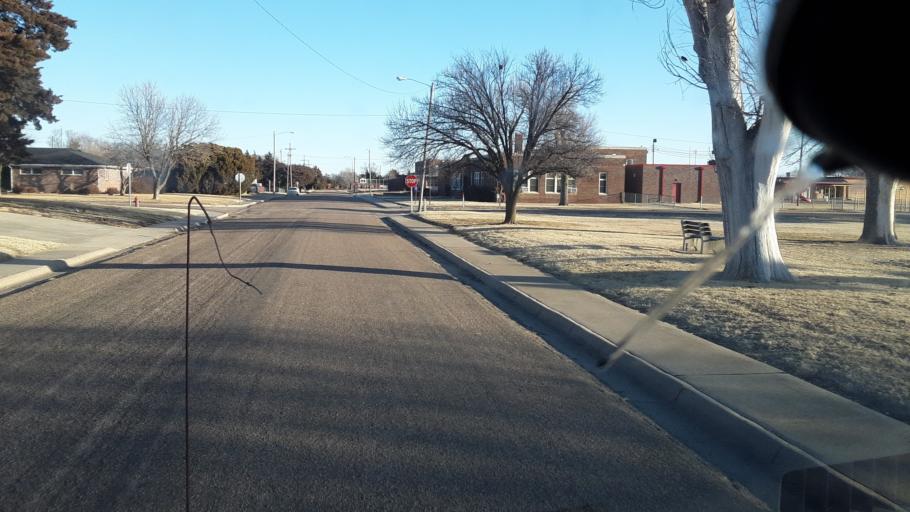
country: US
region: Kansas
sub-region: Rice County
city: Lyons
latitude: 38.3546
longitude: -98.3467
